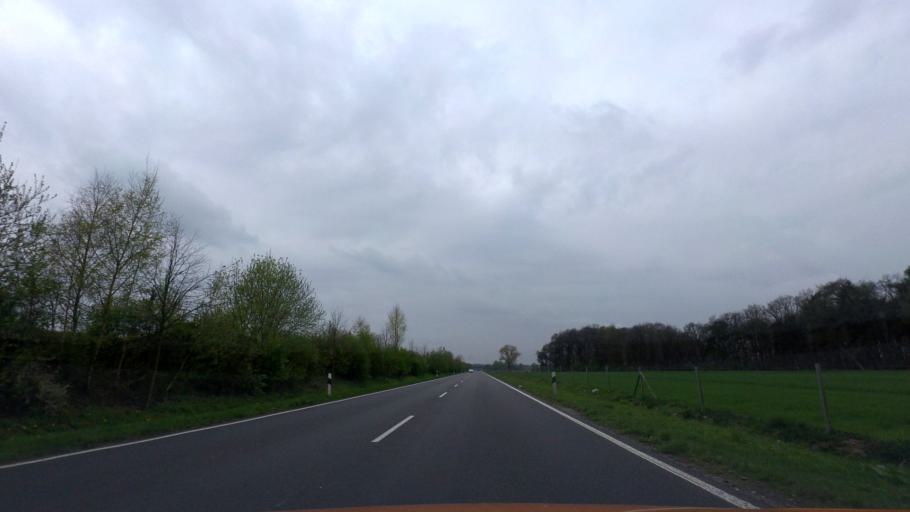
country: DE
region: Lower Saxony
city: Vechta
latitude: 52.7446
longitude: 8.2582
